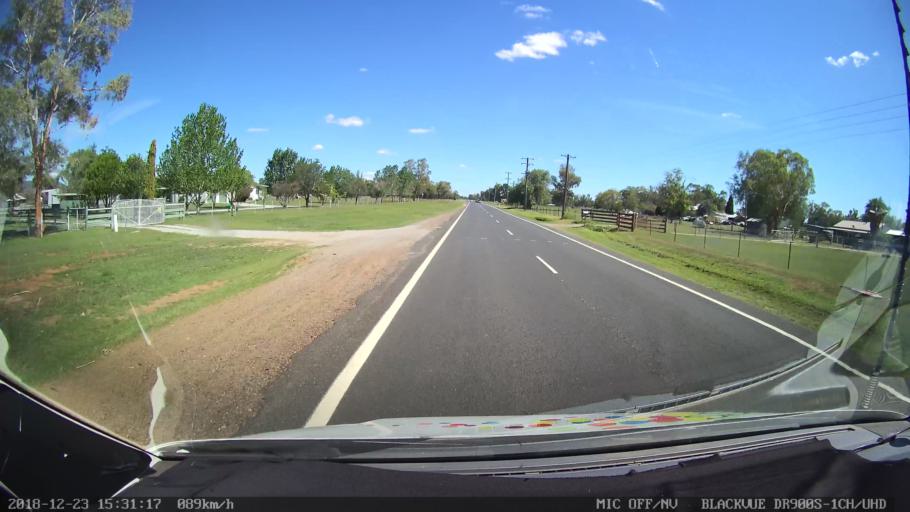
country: AU
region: New South Wales
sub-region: Tamworth Municipality
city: East Tamworth
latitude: -30.9699
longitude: 150.8669
